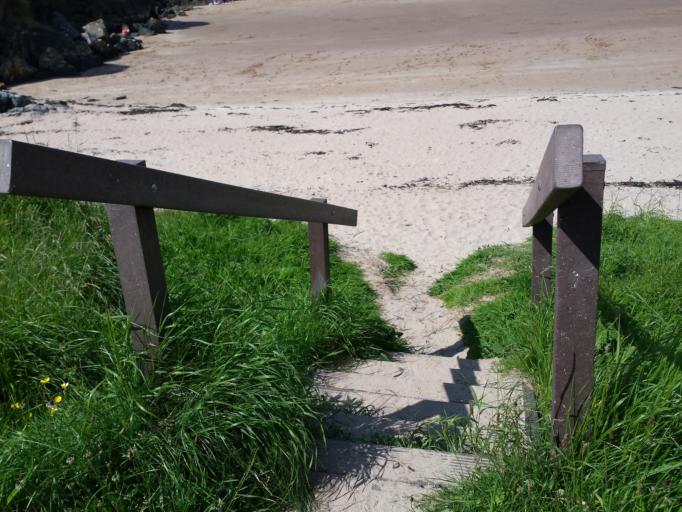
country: GB
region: Scotland
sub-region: Highland
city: Ullapool
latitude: 57.7138
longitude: -5.6897
